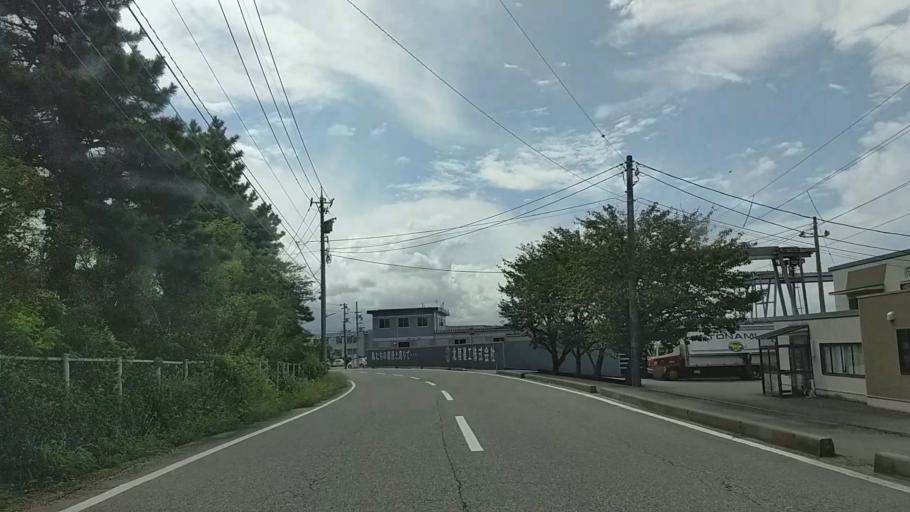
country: JP
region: Toyama
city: Kamiichi
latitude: 36.7436
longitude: 137.3769
